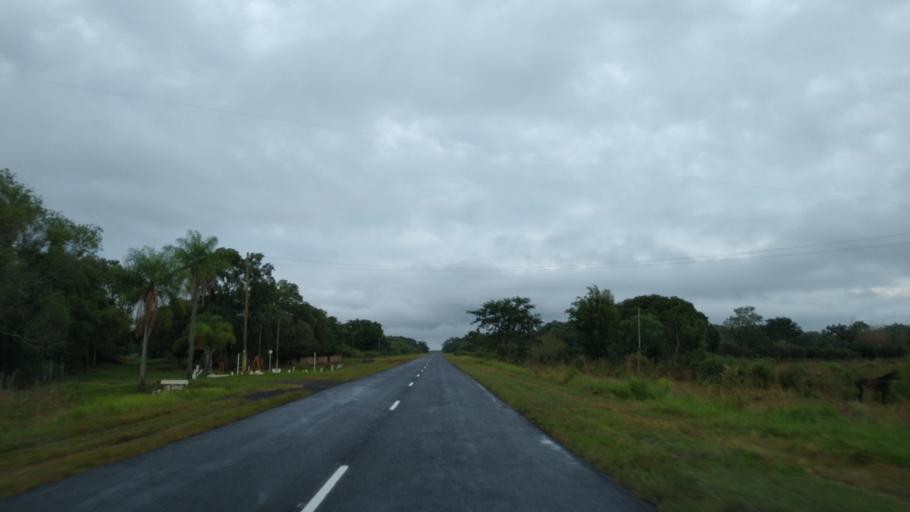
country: AR
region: Corrientes
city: Loreto
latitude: -27.7404
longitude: -57.2486
